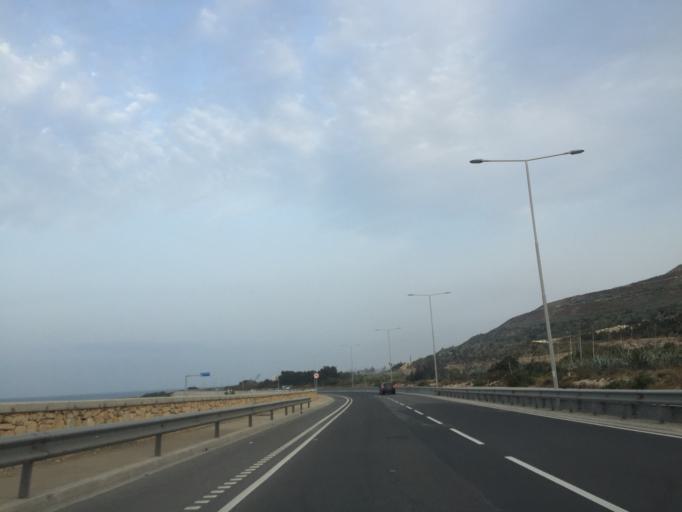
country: MT
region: Saint Paul's Bay
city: San Pawl il-Bahar
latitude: 35.9522
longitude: 14.4395
